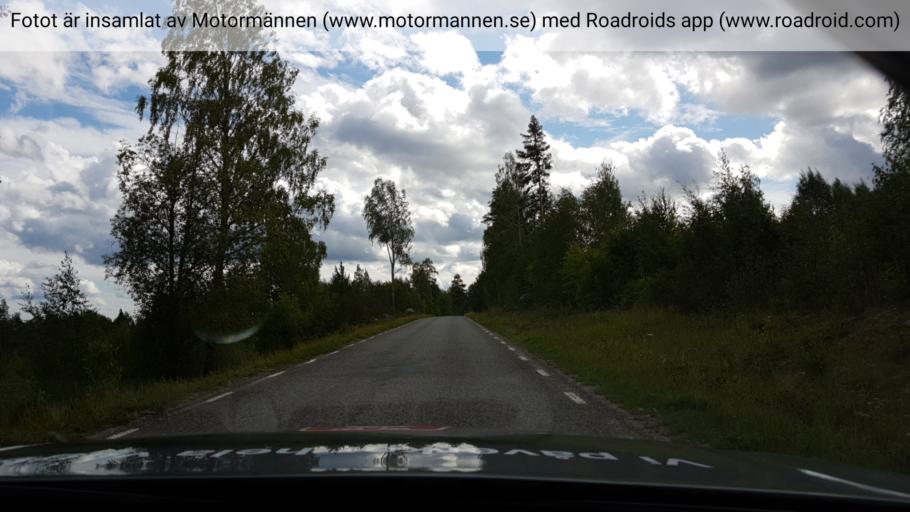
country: SE
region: Jaemtland
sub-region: OEstersunds Kommun
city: Lit
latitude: 63.2333
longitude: 15.2528
